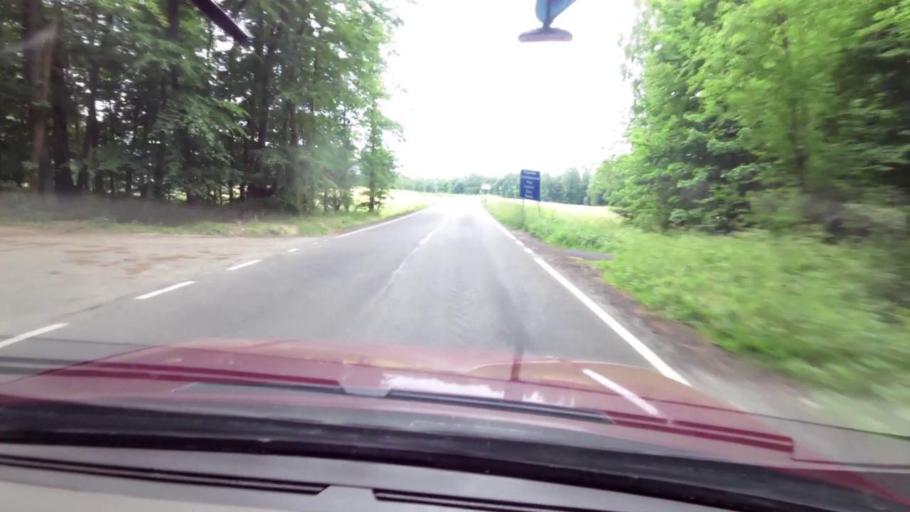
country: PL
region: West Pomeranian Voivodeship
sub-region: Powiat koszalinski
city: Polanow
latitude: 54.1666
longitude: 16.7530
